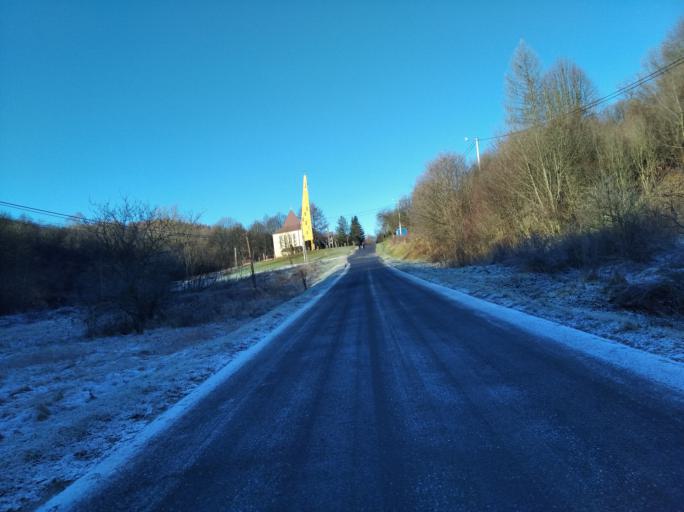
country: PL
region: Subcarpathian Voivodeship
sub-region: Powiat strzyzowski
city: Czudec
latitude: 49.9541
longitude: 21.7691
